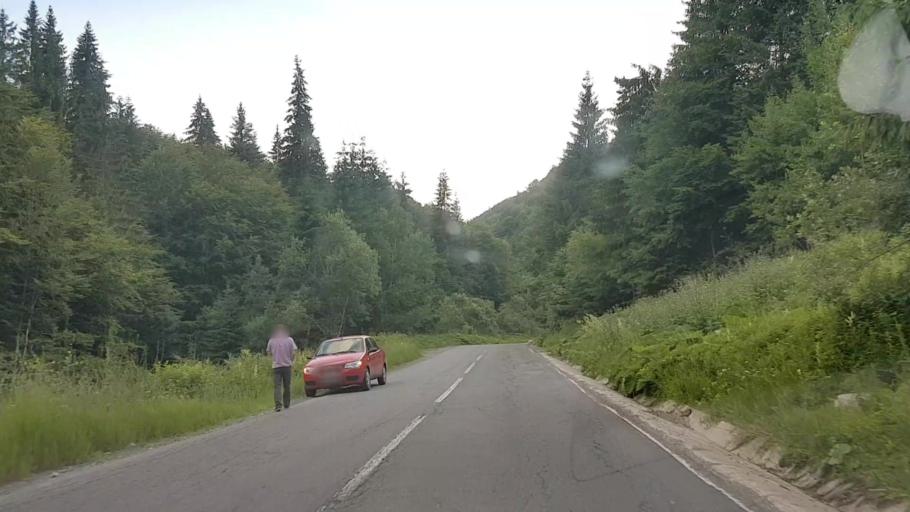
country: RO
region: Harghita
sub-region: Comuna Praid
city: Ocna de Sus
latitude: 46.6235
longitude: 25.2534
